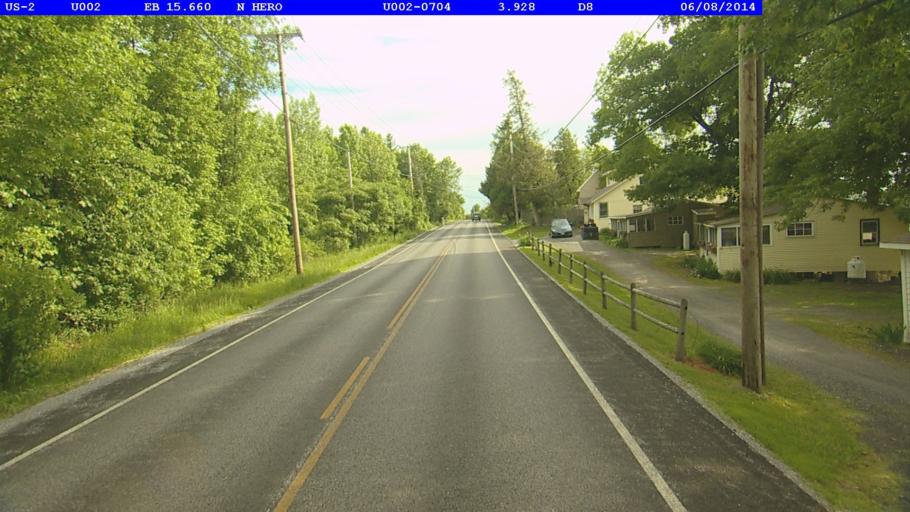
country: US
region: Vermont
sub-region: Grand Isle County
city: North Hero
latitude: 44.8360
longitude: -73.2714
